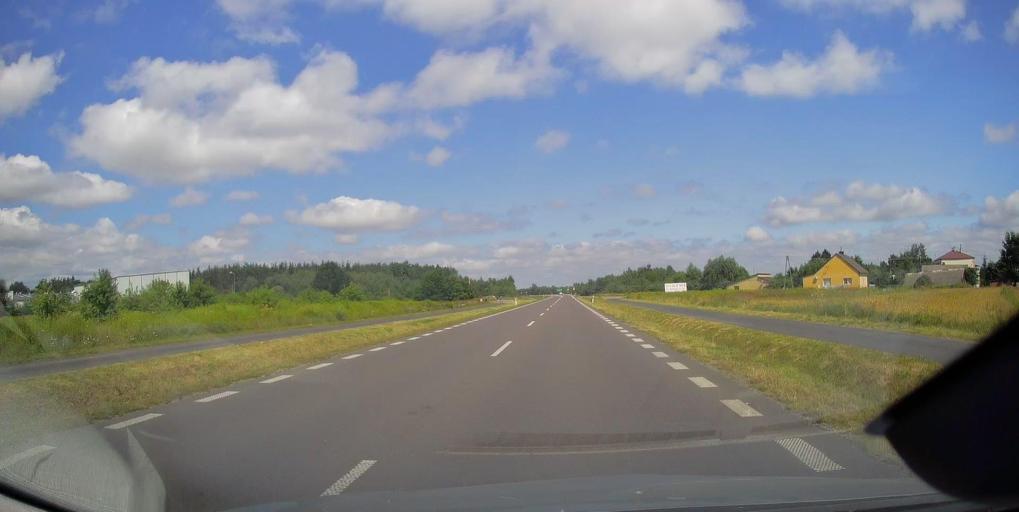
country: PL
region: Subcarpathian Voivodeship
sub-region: Powiat mielecki
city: Padew Narodowa
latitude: 50.3478
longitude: 21.4941
